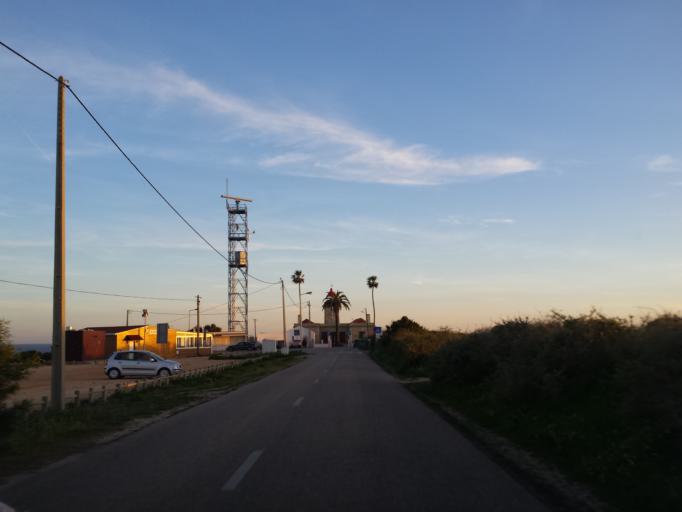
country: PT
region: Faro
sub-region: Lagos
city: Lagos
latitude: 37.0819
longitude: -8.6699
